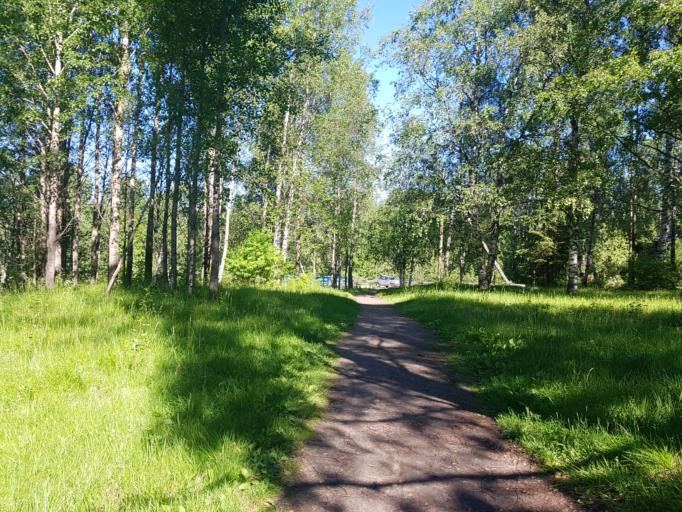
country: RU
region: Republic of Karelia
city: Kalevala
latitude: 65.1971
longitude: 31.1872
